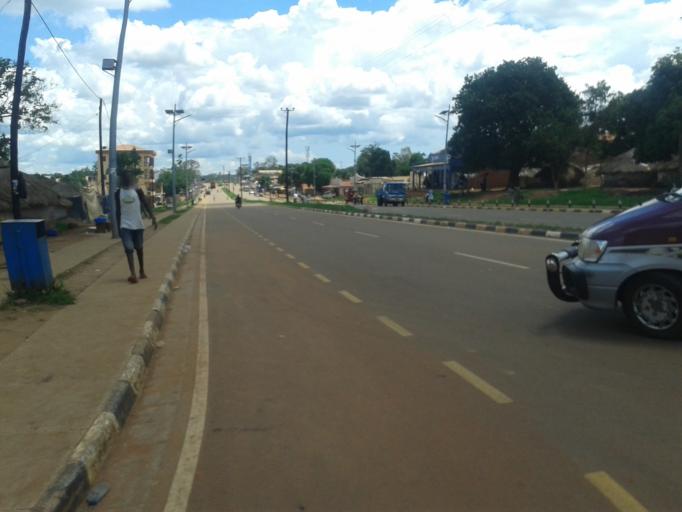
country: UG
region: Northern Region
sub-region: Gulu District
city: Gulu
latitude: 2.7648
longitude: 32.3032
